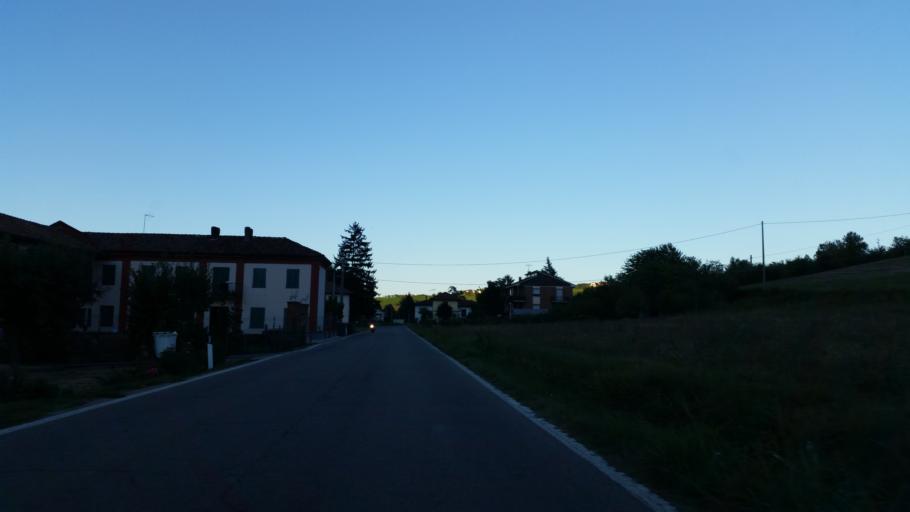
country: IT
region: Piedmont
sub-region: Provincia di Cuneo
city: Neive-Borgonovo
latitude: 44.7105
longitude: 8.1102
